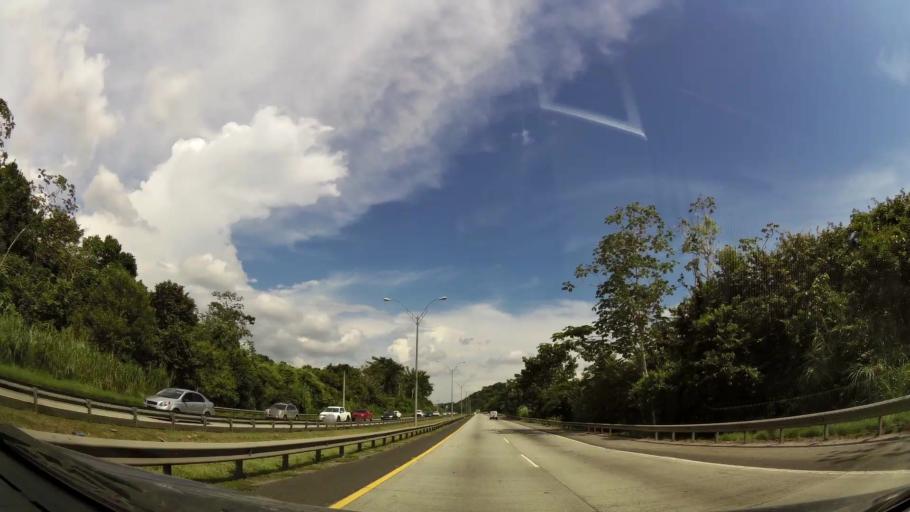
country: PA
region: Panama
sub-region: Distrito de Panama
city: Paraiso
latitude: 9.0275
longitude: -79.5966
